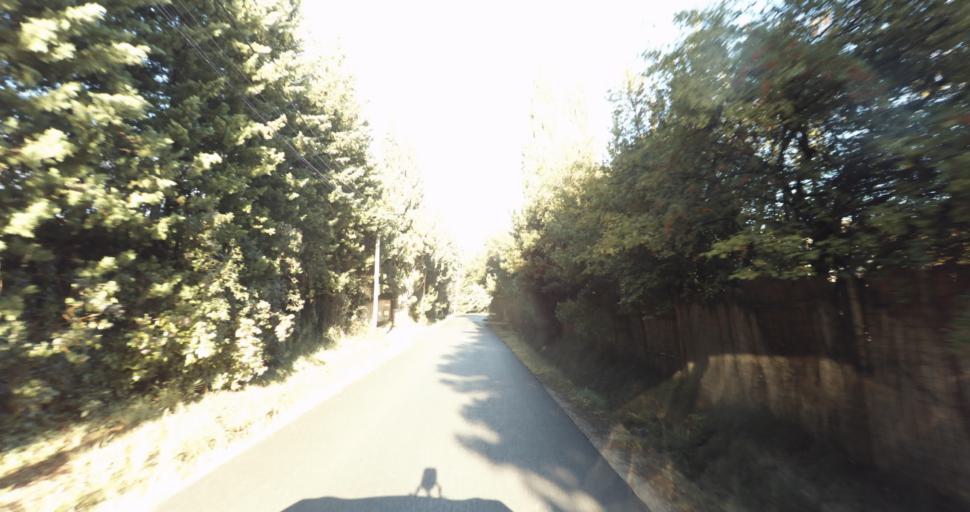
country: FR
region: Provence-Alpes-Cote d'Azur
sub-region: Departement des Bouches-du-Rhone
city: Rognonas
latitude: 43.8795
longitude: 4.7991
